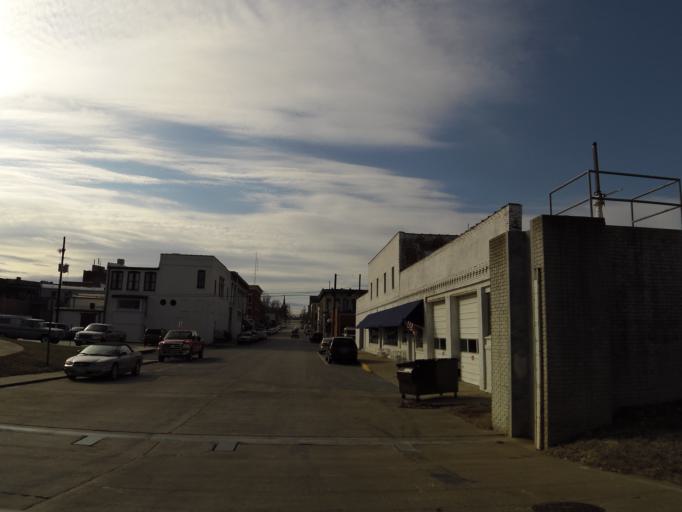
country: US
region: Missouri
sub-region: Marion County
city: Hannibal
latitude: 39.7110
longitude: -91.3551
